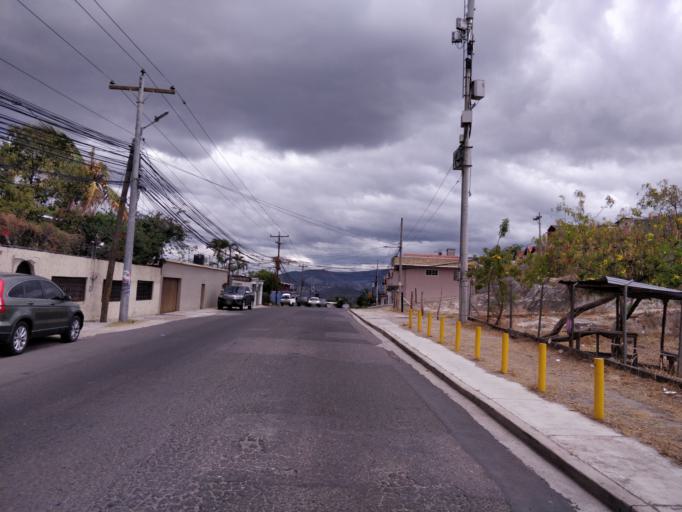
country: HN
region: Francisco Morazan
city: Yaguacire
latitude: 14.0486
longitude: -87.2199
